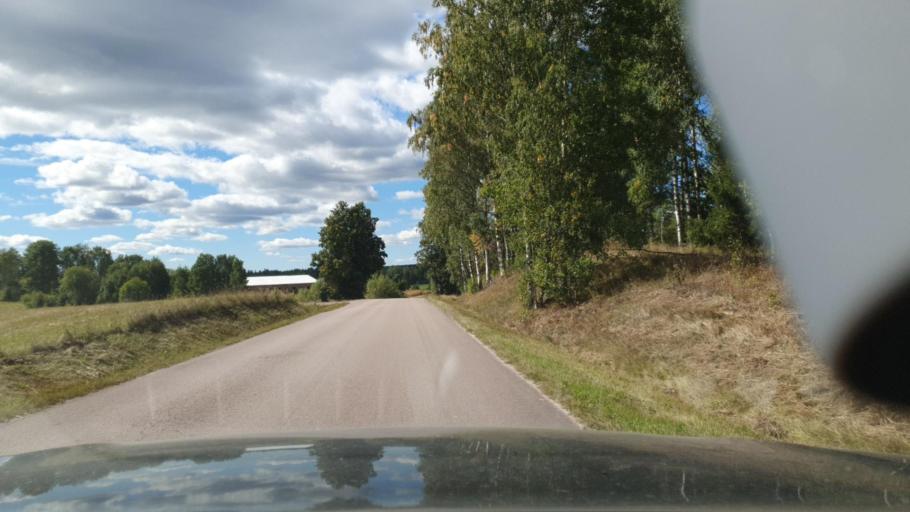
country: SE
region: Vaermland
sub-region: Karlstads Kommun
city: Molkom
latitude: 59.5591
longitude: 13.7015
